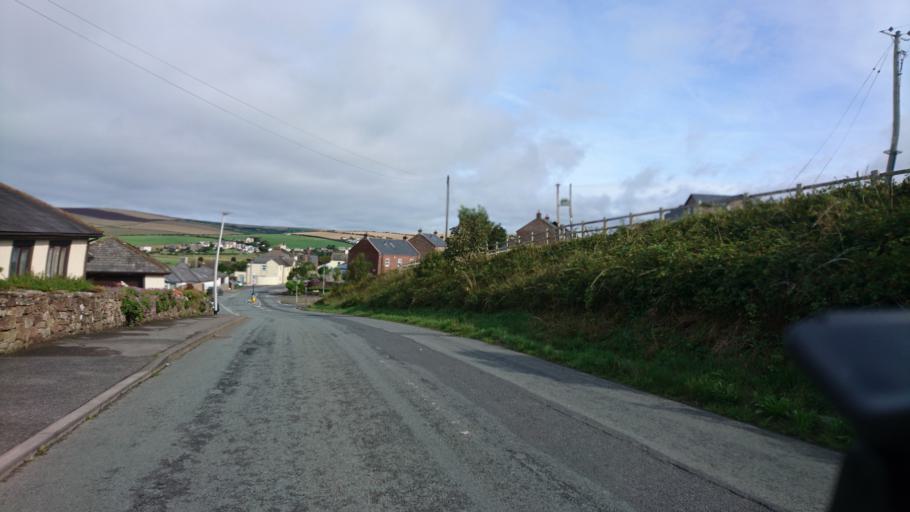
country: GB
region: England
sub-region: Cumbria
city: Saint Bees
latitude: 54.4853
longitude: -3.5883
